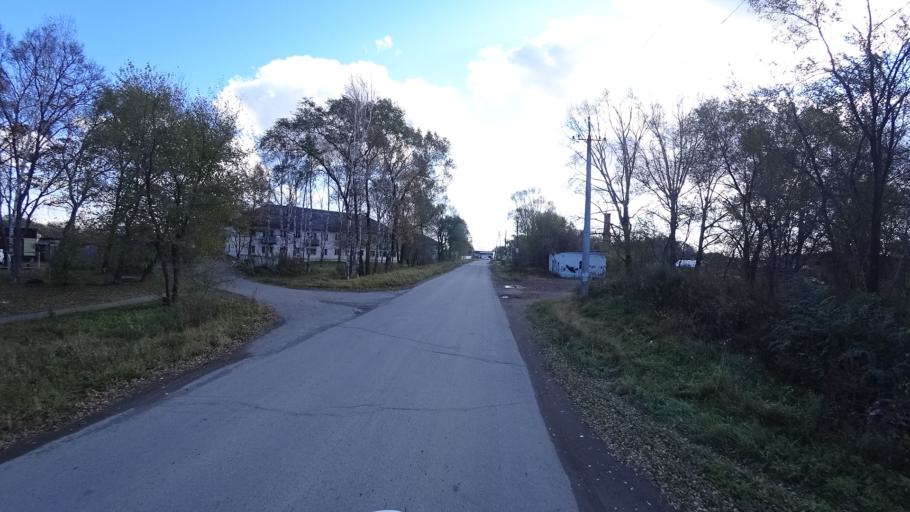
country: RU
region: Khabarovsk Krai
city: Amursk
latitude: 50.0953
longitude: 136.4986
